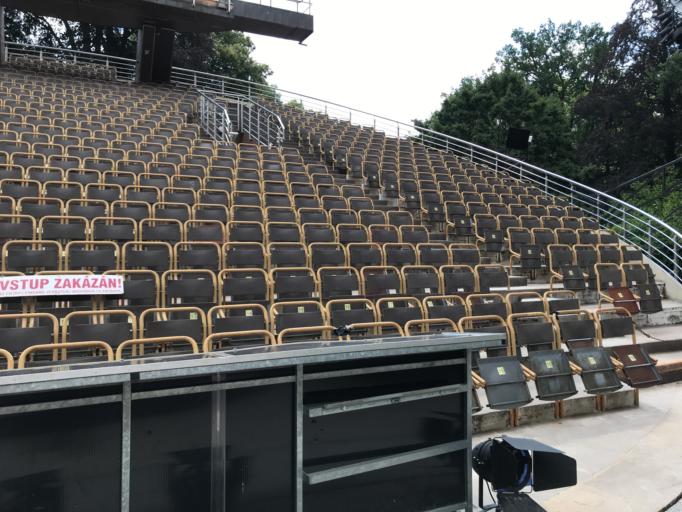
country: CZ
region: Jihocesky
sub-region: Okres Cesky Krumlov
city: Cesky Krumlov
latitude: 48.8106
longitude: 14.3075
